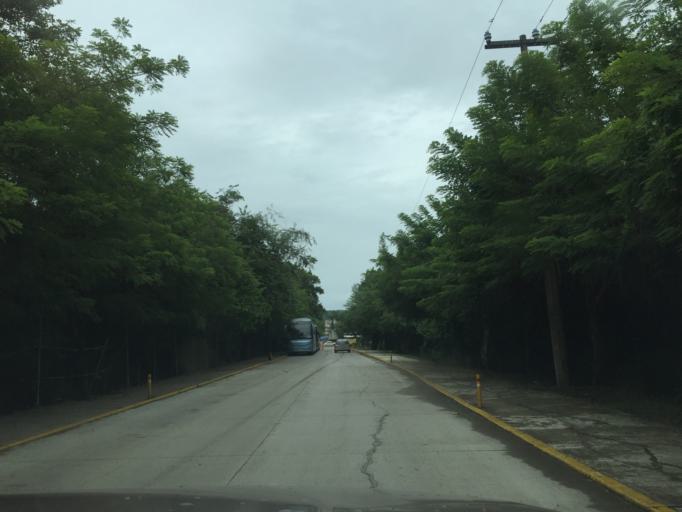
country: MX
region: Veracruz
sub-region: Papantla
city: El Chote
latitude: 20.4393
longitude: -97.3786
